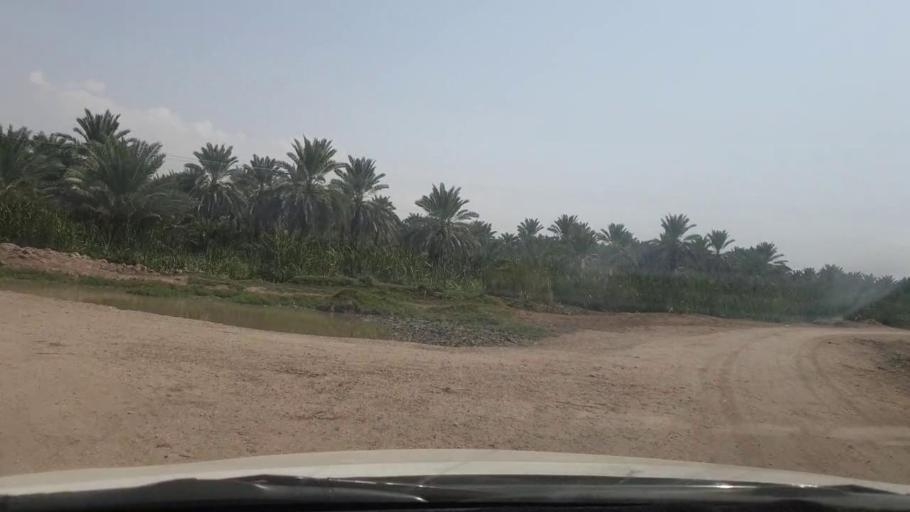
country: PK
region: Sindh
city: Khairpur
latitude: 27.5541
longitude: 68.8388
